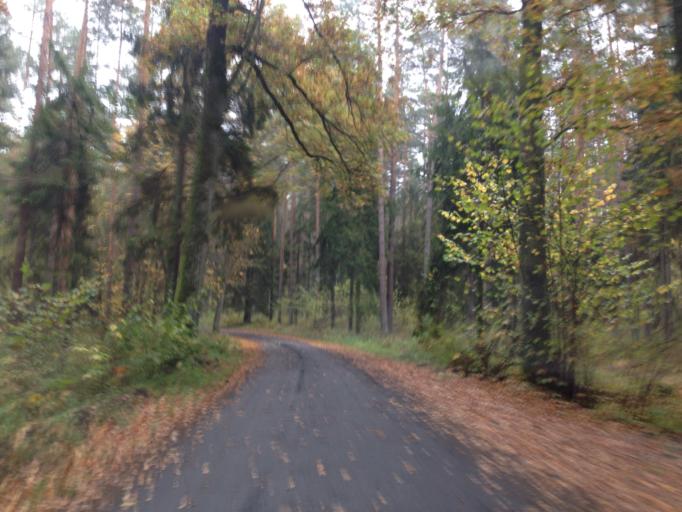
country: PL
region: Kujawsko-Pomorskie
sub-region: Powiat brodnicki
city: Gorzno
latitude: 53.2236
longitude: 19.6911
